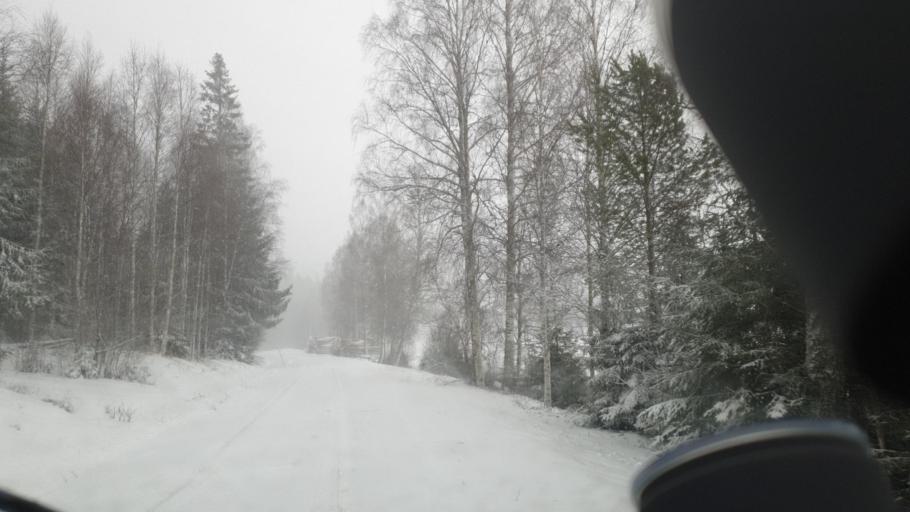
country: SE
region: Vaermland
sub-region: Arvika Kommun
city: Arvika
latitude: 59.8113
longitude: 12.7466
